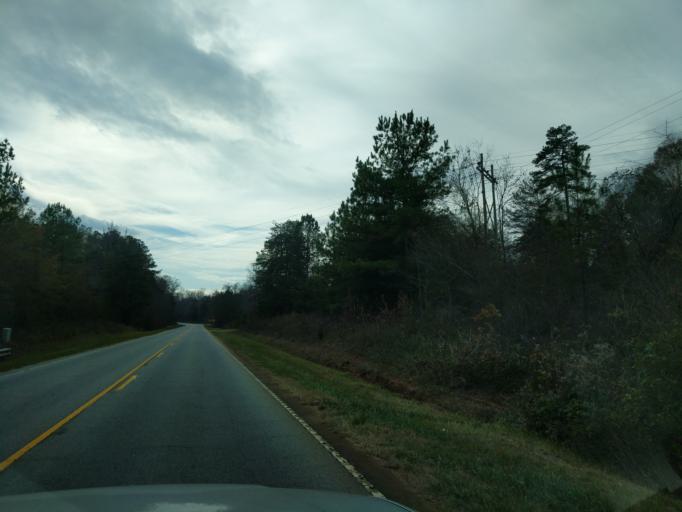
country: US
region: South Carolina
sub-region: Oconee County
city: Utica
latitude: 34.7589
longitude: -82.9029
